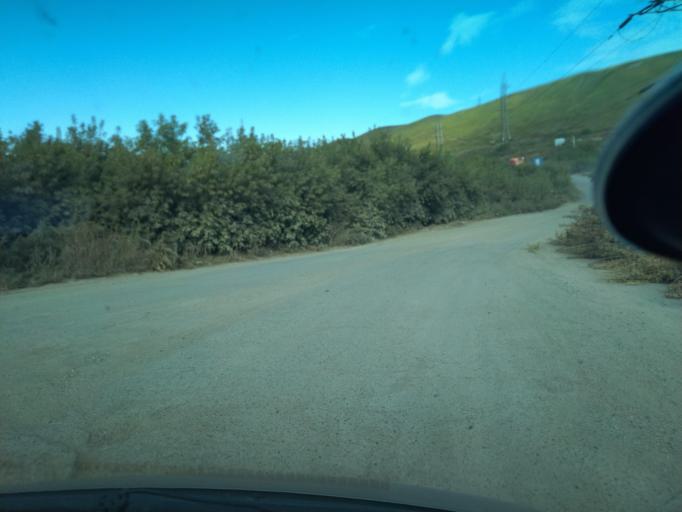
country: RU
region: Krasnoyarskiy
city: Krasnoyarsk
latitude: 55.9754
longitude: 92.9436
